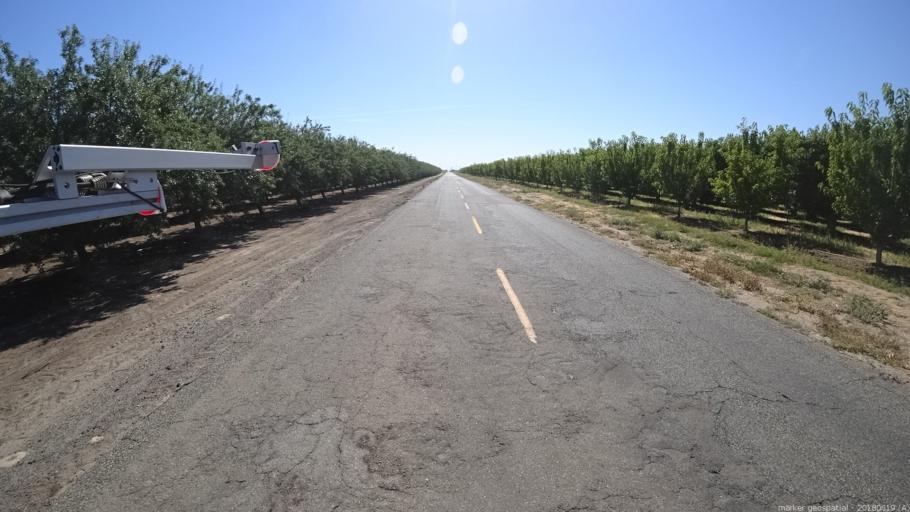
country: US
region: California
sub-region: Fresno County
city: Biola
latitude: 36.8368
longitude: -120.0871
